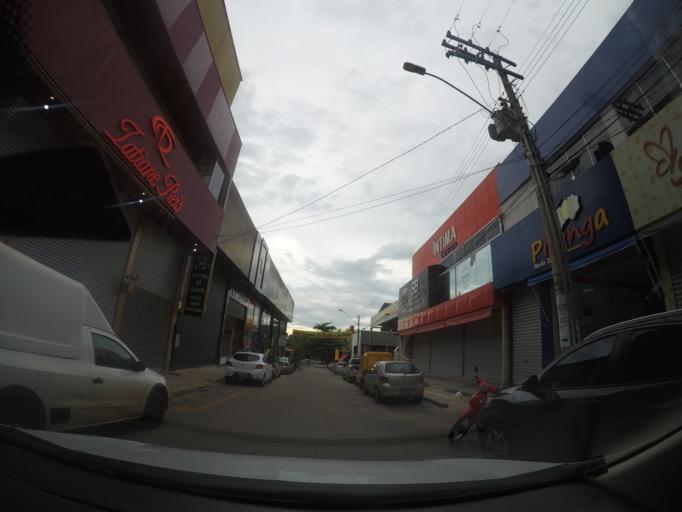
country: BR
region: Goias
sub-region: Goiania
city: Goiania
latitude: -16.6603
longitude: -49.2547
